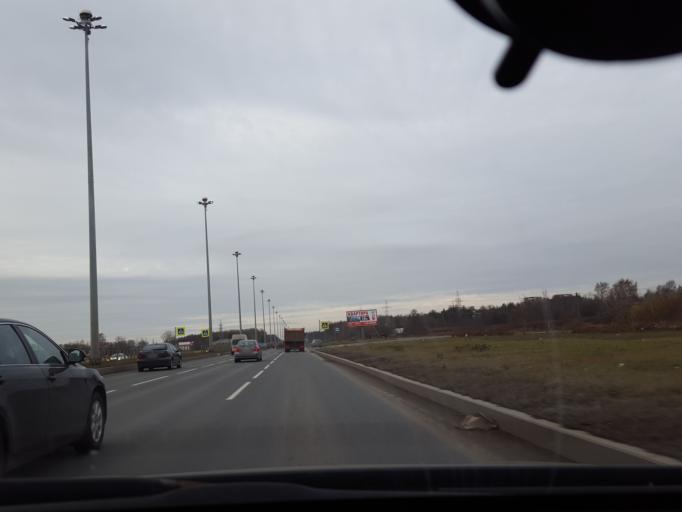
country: RU
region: Leningrad
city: Untolovo
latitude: 60.0404
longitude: 30.2416
